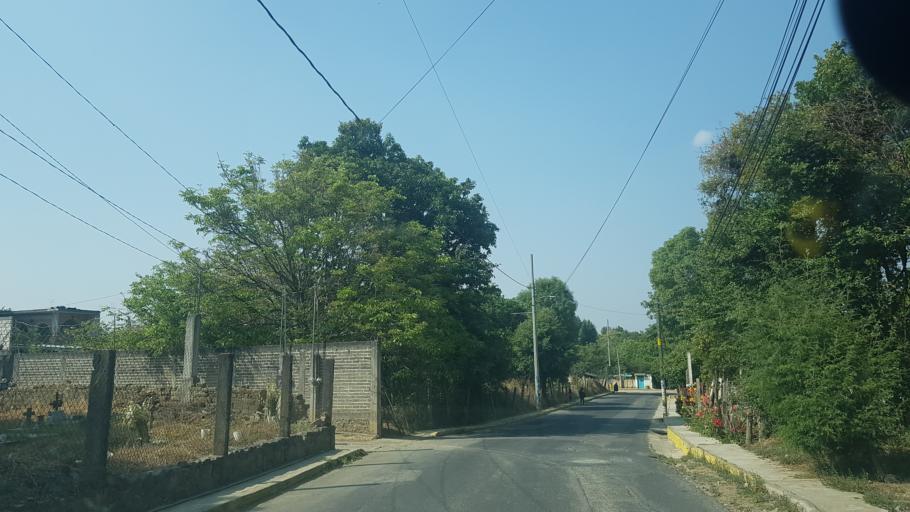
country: MX
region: Morelos
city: Hueyapan
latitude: 18.8805
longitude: -98.6930
